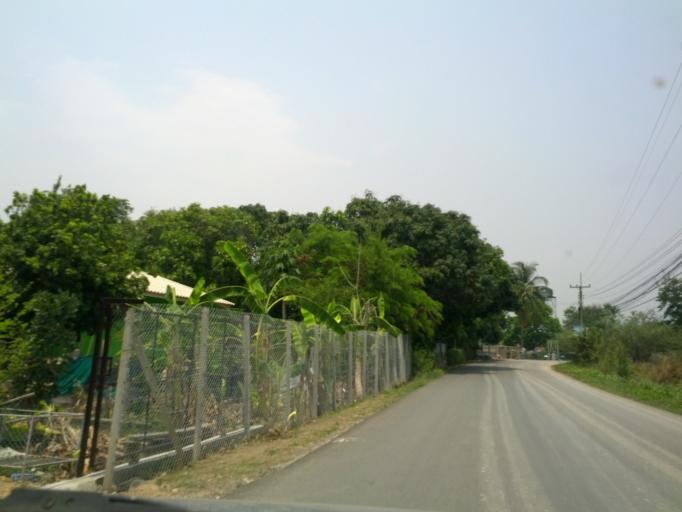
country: TH
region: Chiang Mai
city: San Sai
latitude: 18.8982
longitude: 99.0341
